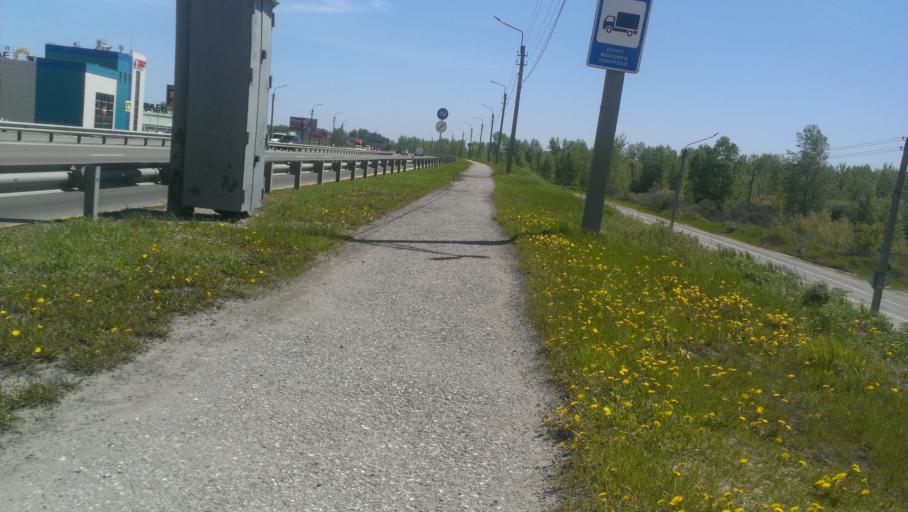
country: RU
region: Altai Krai
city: Zaton
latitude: 53.3167
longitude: 83.8228
